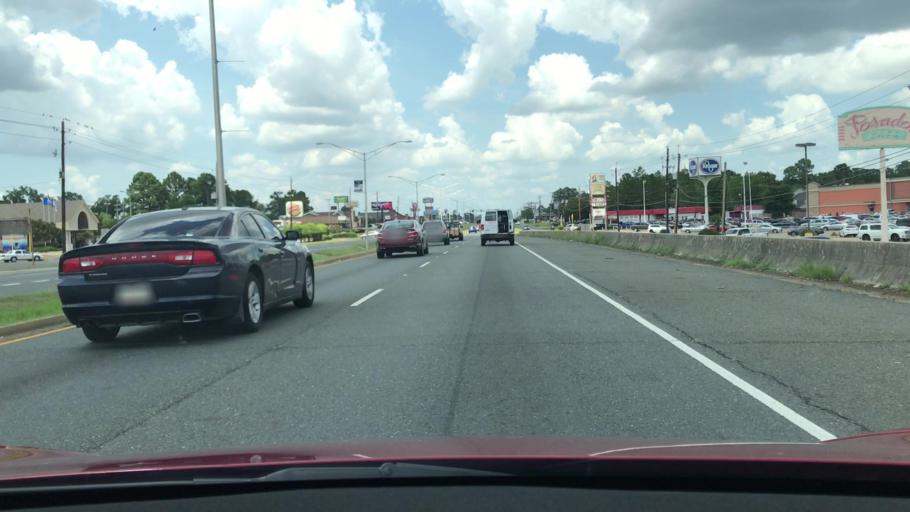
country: US
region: Louisiana
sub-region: De Soto Parish
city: Stonewall
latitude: 32.4030
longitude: -93.8033
